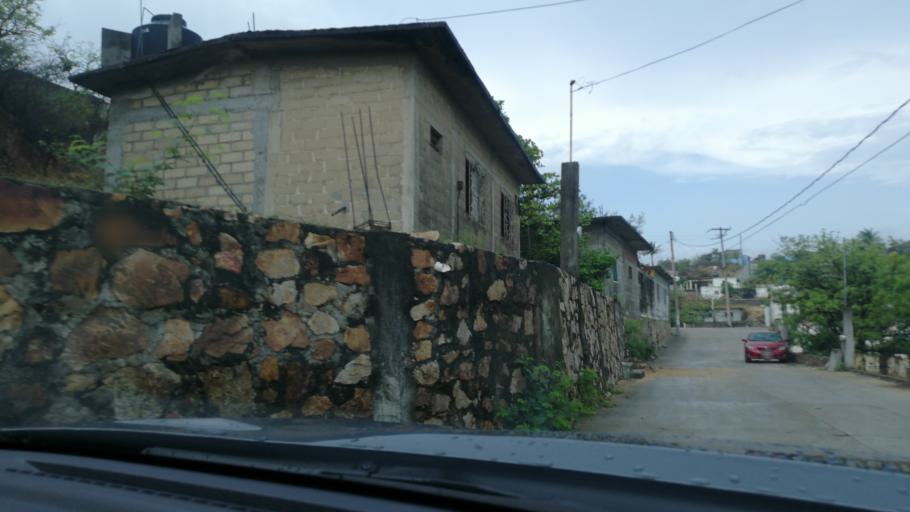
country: MX
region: Oaxaca
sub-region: Salina Cruz
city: Salina Cruz
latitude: 16.1881
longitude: -95.1955
